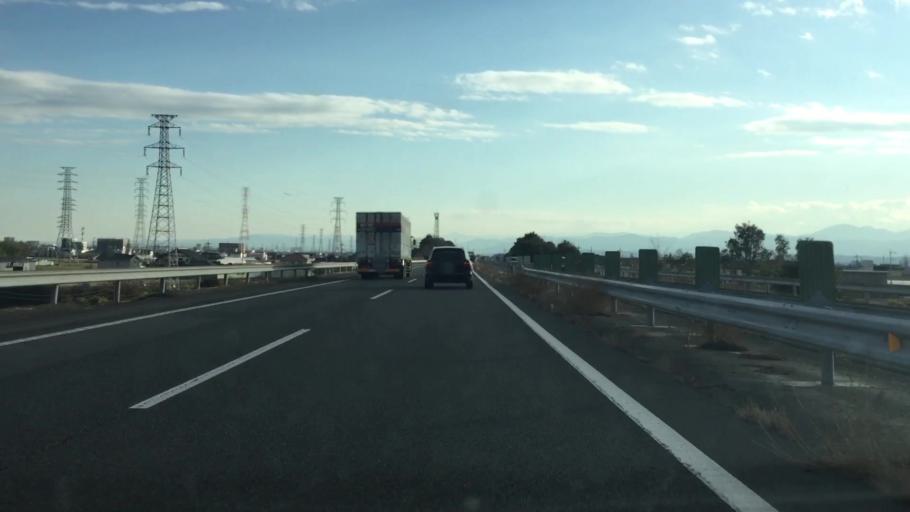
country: JP
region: Gunma
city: Kanekomachi
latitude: 36.4018
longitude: 139.0245
